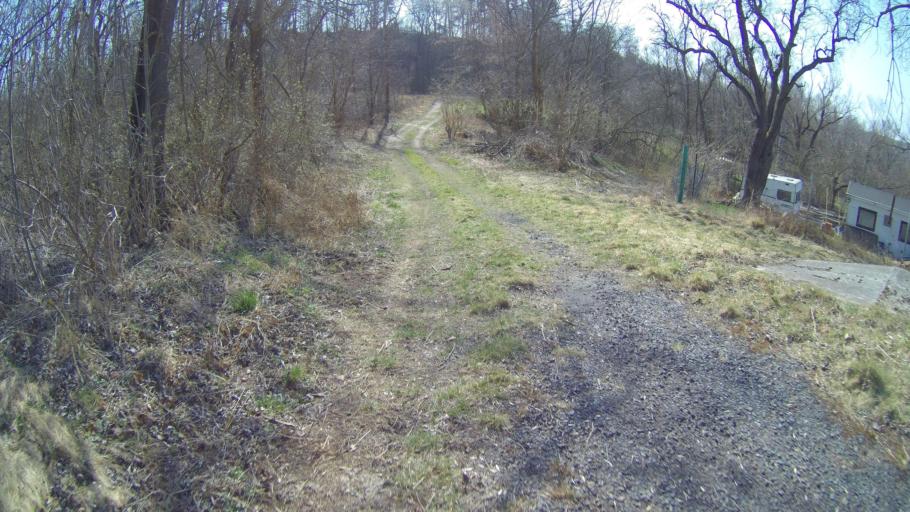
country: CZ
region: Ustecky
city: Mecholupy
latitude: 50.2881
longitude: 13.5760
